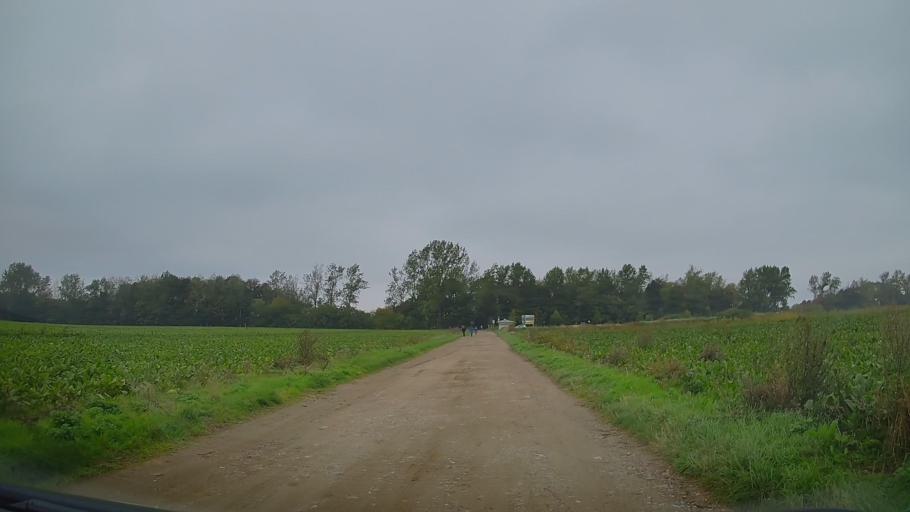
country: DE
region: Mecklenburg-Vorpommern
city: Bastorf
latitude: 54.1133
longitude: 11.6261
